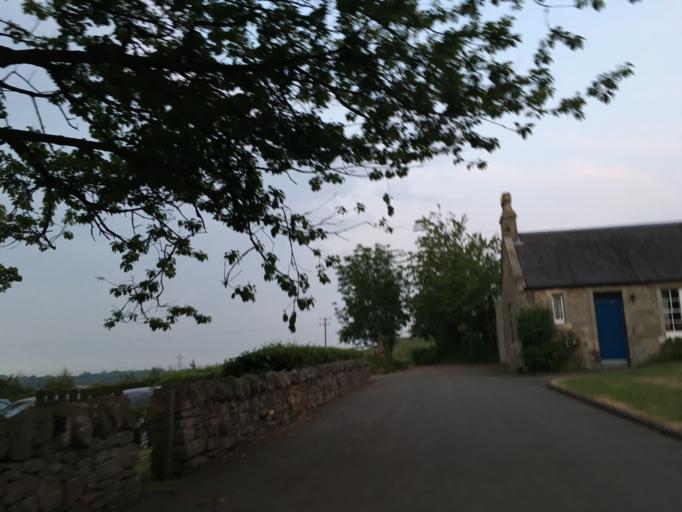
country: GB
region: Scotland
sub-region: Edinburgh
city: Colinton
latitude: 55.8926
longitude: -3.2155
